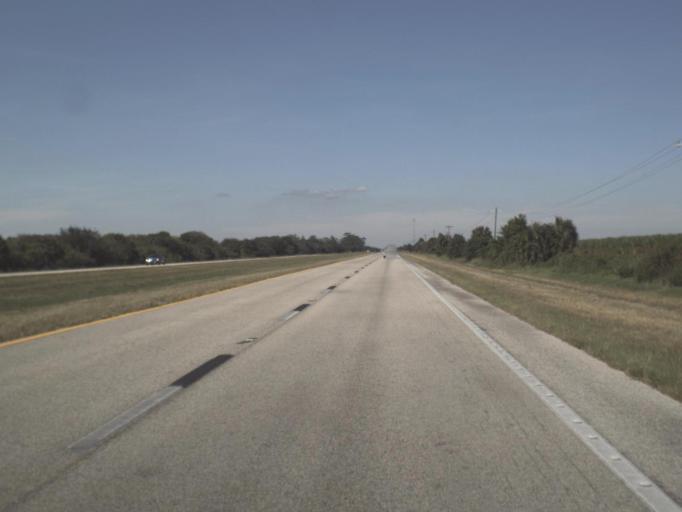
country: US
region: Florida
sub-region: Glades County
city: Moore Haven
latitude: 26.8495
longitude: -81.2028
